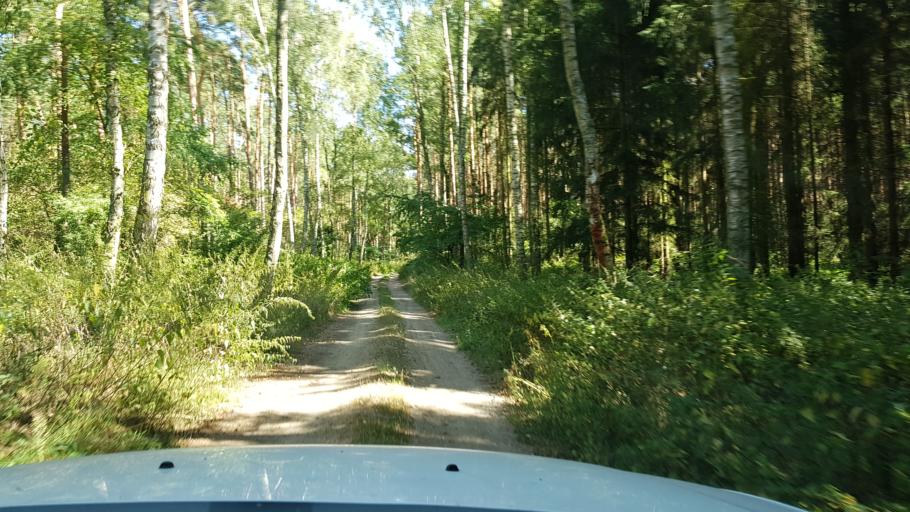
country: PL
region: West Pomeranian Voivodeship
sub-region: Powiat gryfinski
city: Cedynia
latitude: 52.8466
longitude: 14.2364
